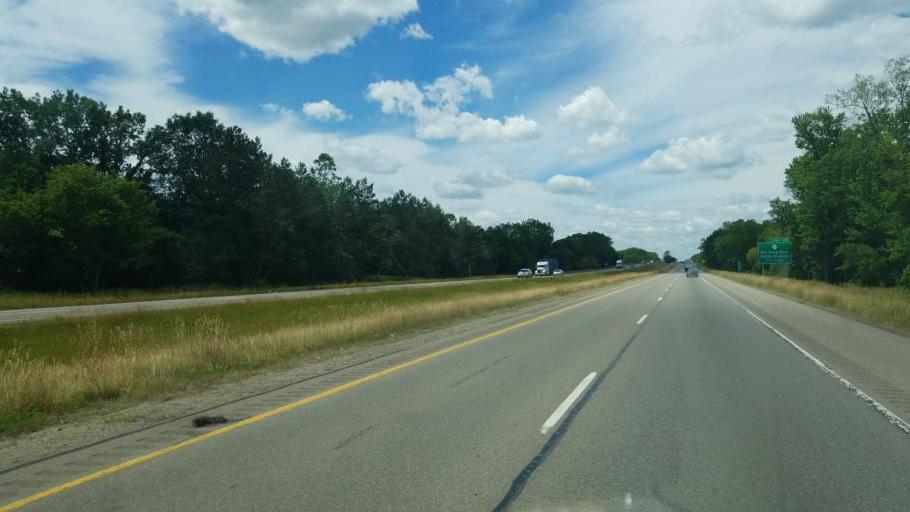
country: US
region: Michigan
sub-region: Ingham County
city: Holt
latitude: 42.6600
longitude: -84.5567
